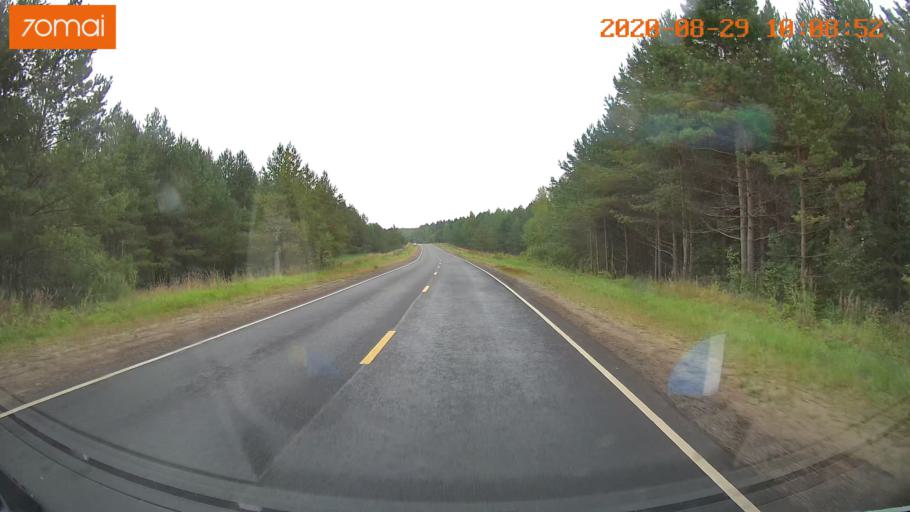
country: RU
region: Ivanovo
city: Kuznechikha
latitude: 57.3743
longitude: 42.6014
